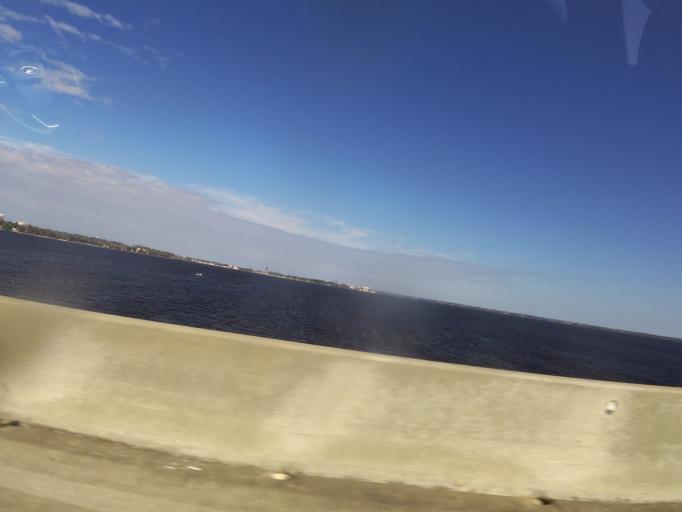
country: US
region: Florida
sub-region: Clay County
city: Orange Park
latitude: 30.1905
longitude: -81.6715
